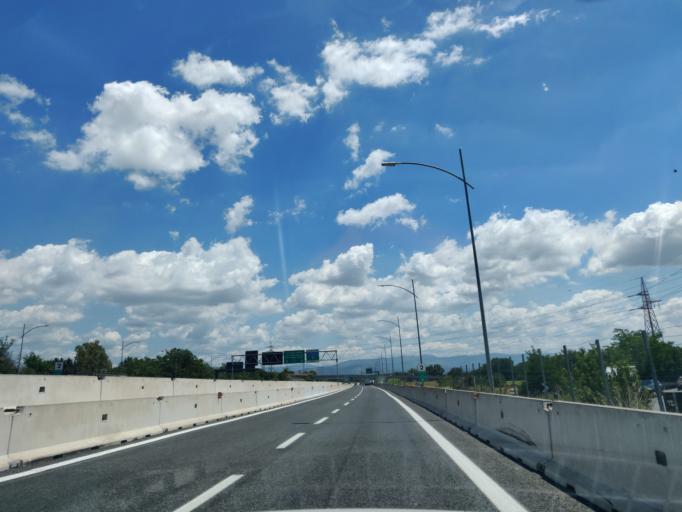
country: IT
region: Latium
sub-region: Citta metropolitana di Roma Capitale
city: Setteville
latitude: 41.9228
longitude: 12.6338
